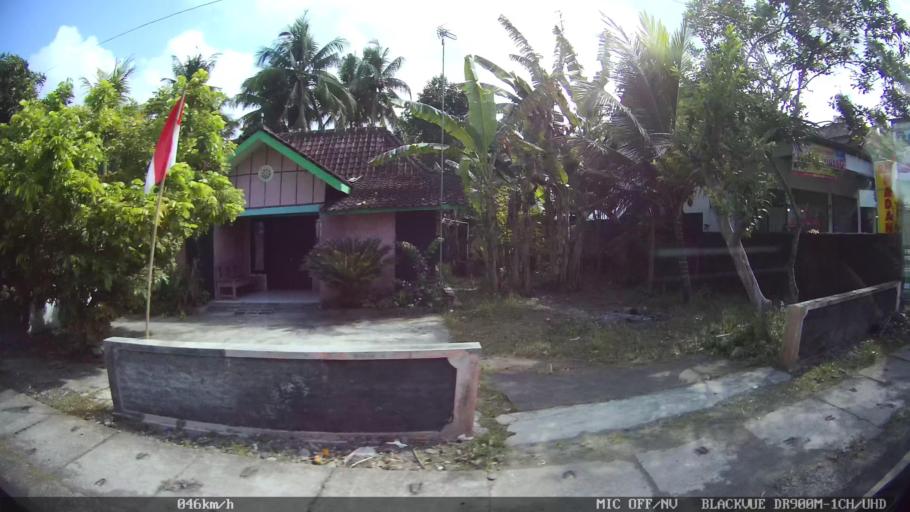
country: ID
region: Daerah Istimewa Yogyakarta
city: Srandakan
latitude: -7.8933
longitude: 110.1390
